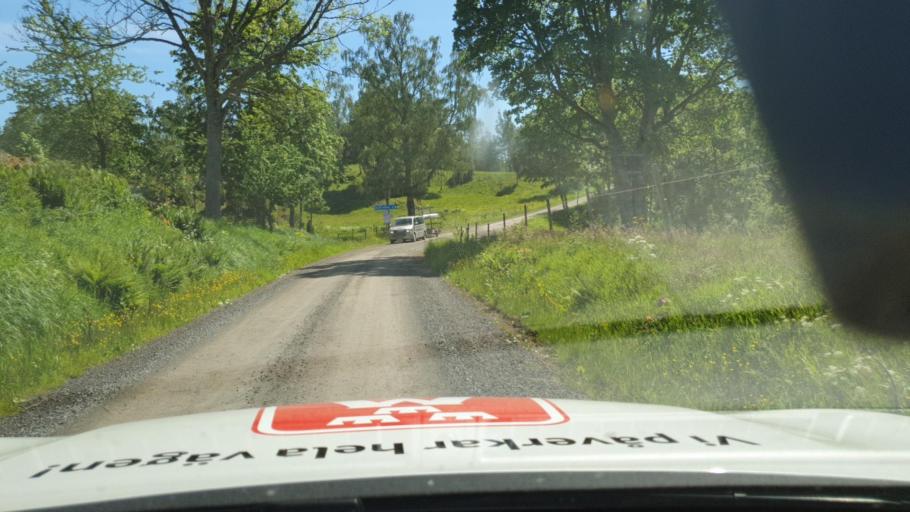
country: SE
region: Joenkoeping
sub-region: Mullsjo Kommun
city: Mullsjoe
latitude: 58.0388
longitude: 13.8792
